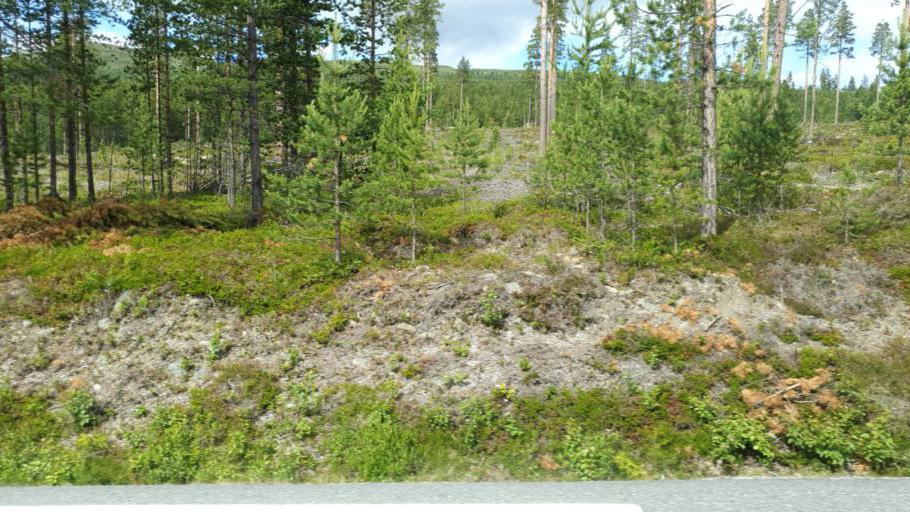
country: NO
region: Oppland
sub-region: Vaga
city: Vagamo
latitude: 61.7342
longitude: 9.0905
